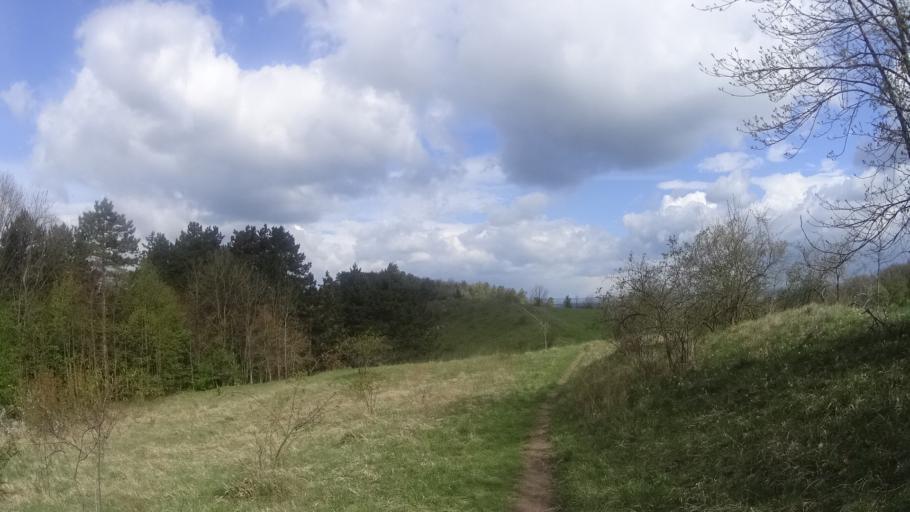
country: DE
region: Thuringia
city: Apfelstadt
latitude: 50.8602
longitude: 10.8778
